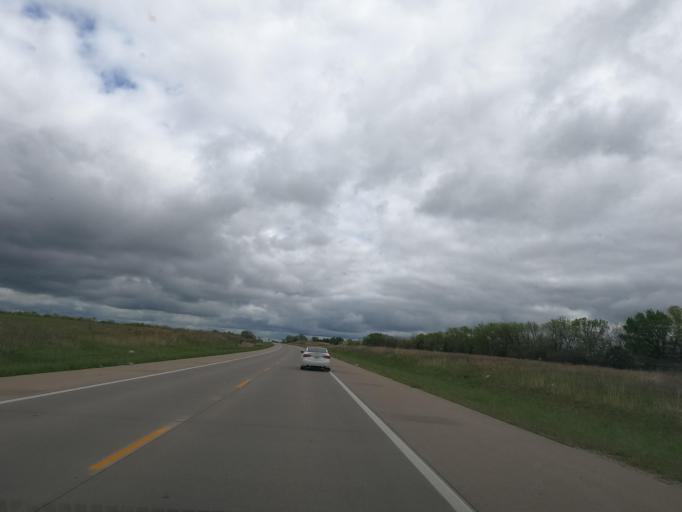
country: US
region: Kansas
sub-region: Montgomery County
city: Cherryvale
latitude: 37.3487
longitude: -95.6067
